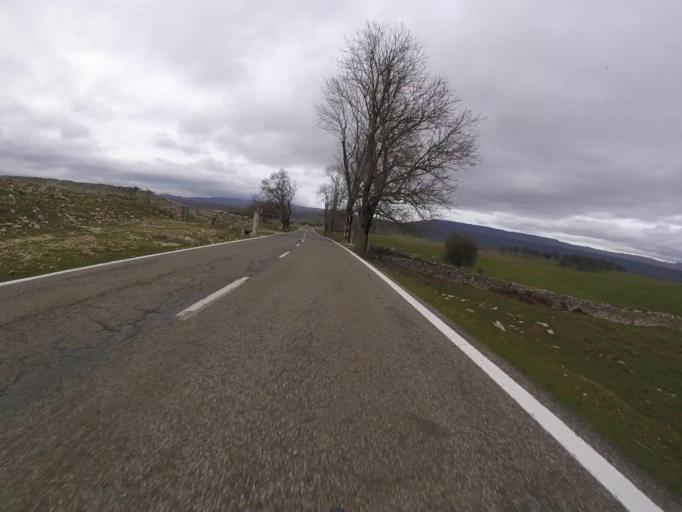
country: ES
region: Navarre
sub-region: Provincia de Navarra
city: Eulate
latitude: 42.8036
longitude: -2.1492
